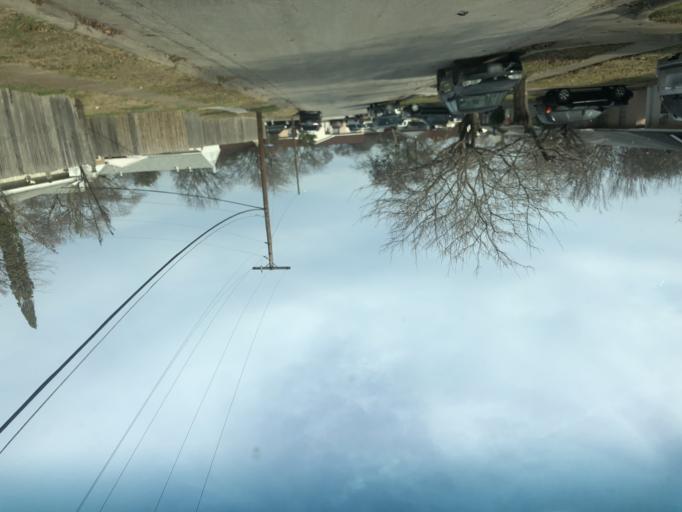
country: US
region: Texas
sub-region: Dallas County
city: Duncanville
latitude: 32.6717
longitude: -96.9013
